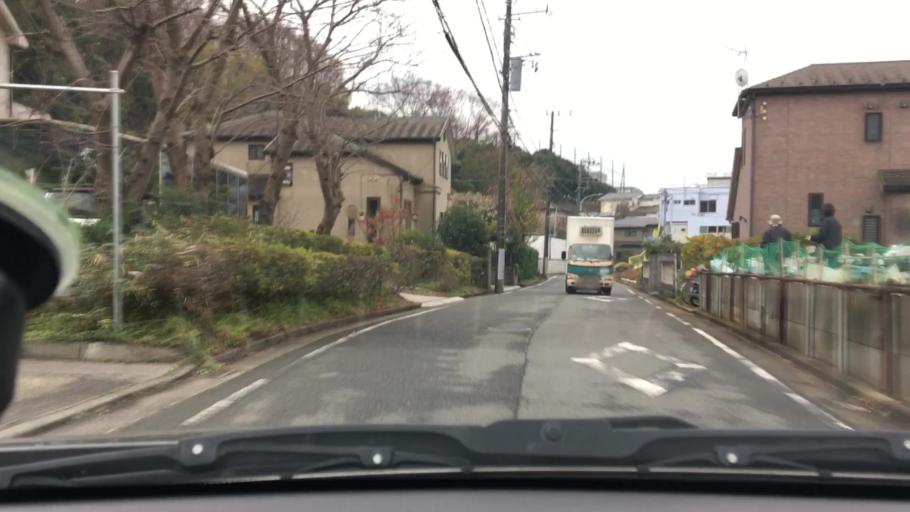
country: JP
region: Kanagawa
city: Yokohama
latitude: 35.5231
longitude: 139.6048
